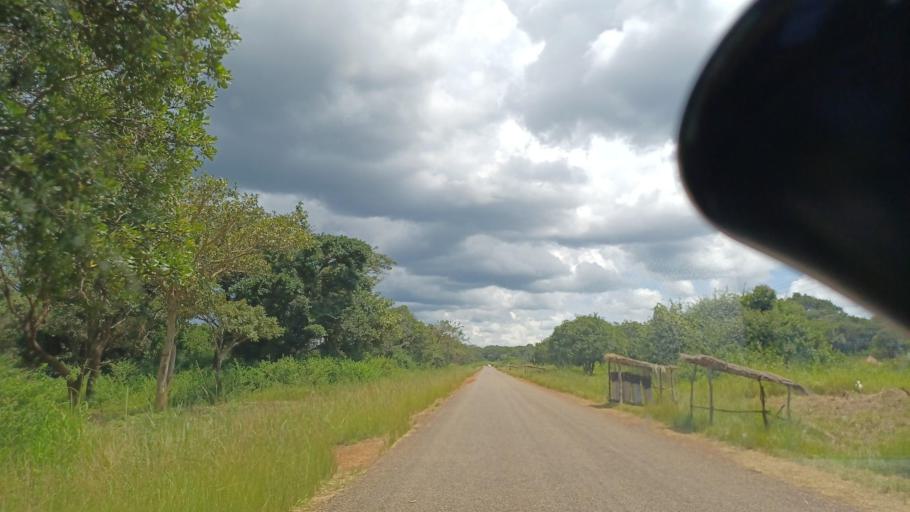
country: ZM
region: North-Western
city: Kasempa
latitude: -12.7752
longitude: 26.0118
